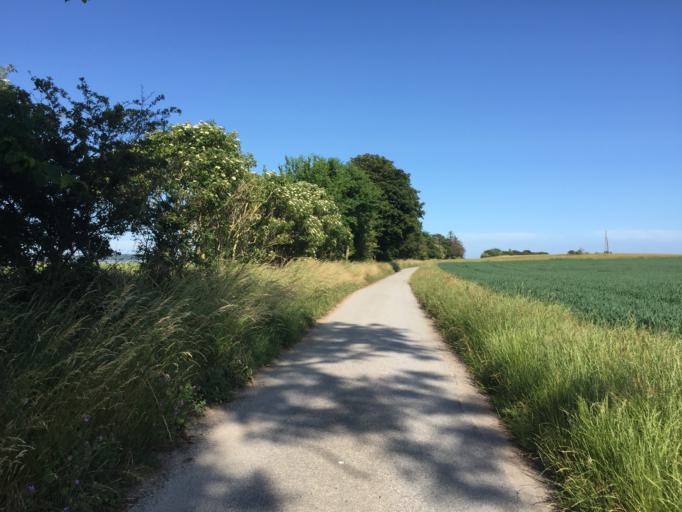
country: DK
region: Zealand
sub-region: Slagelse Kommune
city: Skaelskor
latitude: 55.2012
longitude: 11.1984
